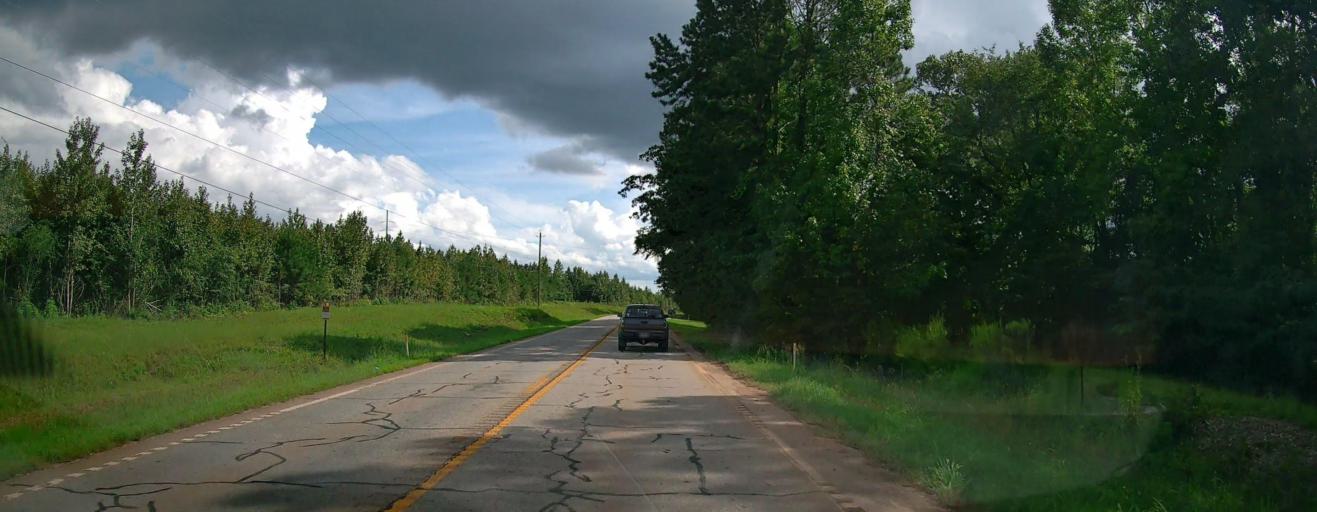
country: US
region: Georgia
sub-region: Harris County
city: Hamilton
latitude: 32.7410
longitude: -84.8700
